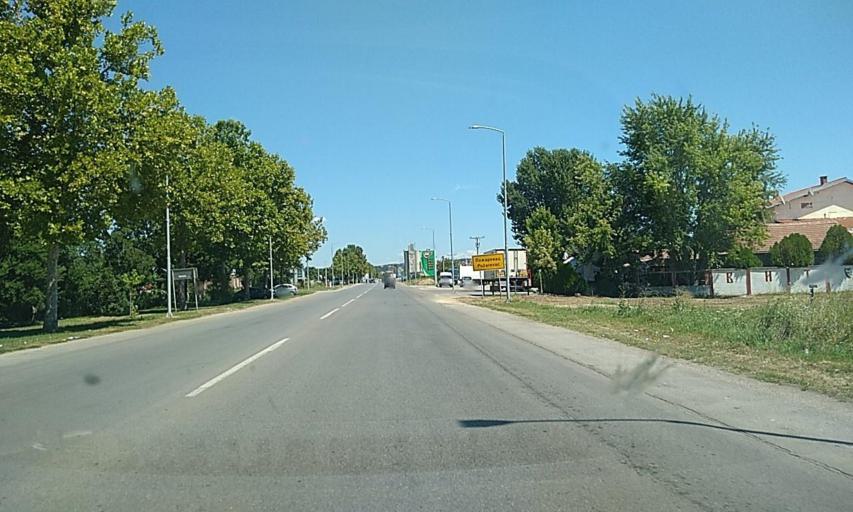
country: RS
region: Central Serbia
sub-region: Branicevski Okrug
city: Pozarevac
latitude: 44.6031
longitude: 21.1616
